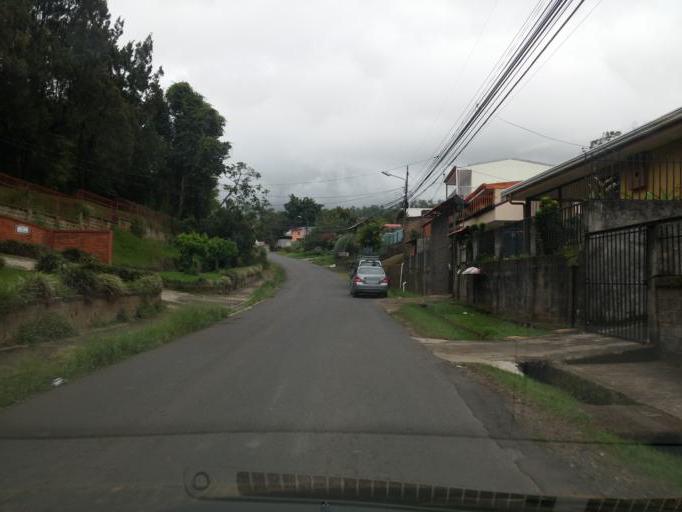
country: CR
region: Heredia
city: Mercedes
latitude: 10.0339
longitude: -84.1322
